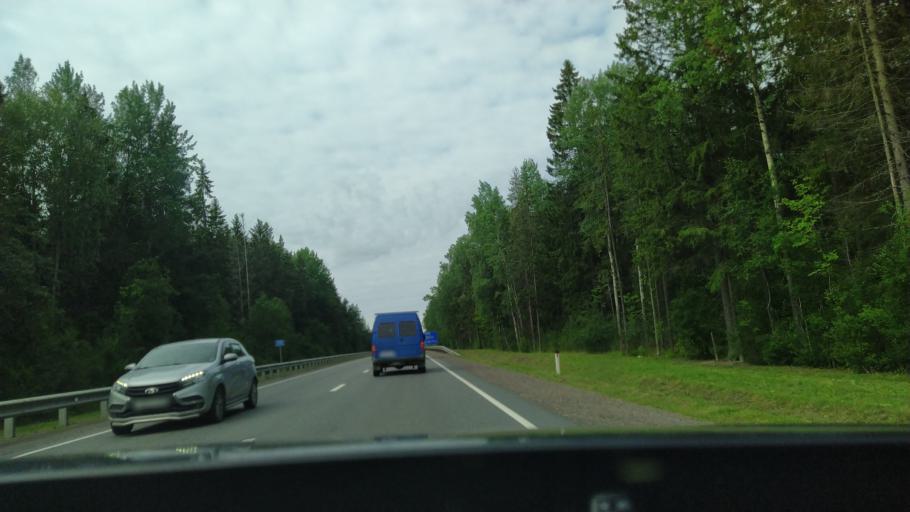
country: RU
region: Leningrad
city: Ul'yanovka
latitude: 59.6118
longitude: 30.7722
